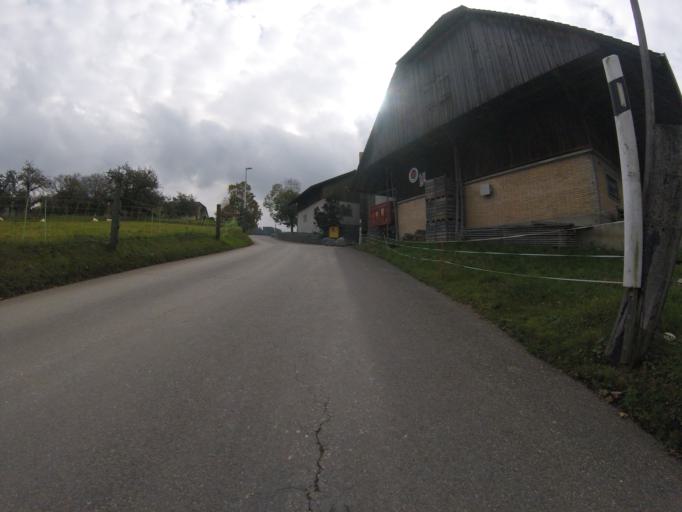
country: CH
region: Bern
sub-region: Bern-Mittelland District
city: Koniz
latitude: 46.8978
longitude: 7.4038
